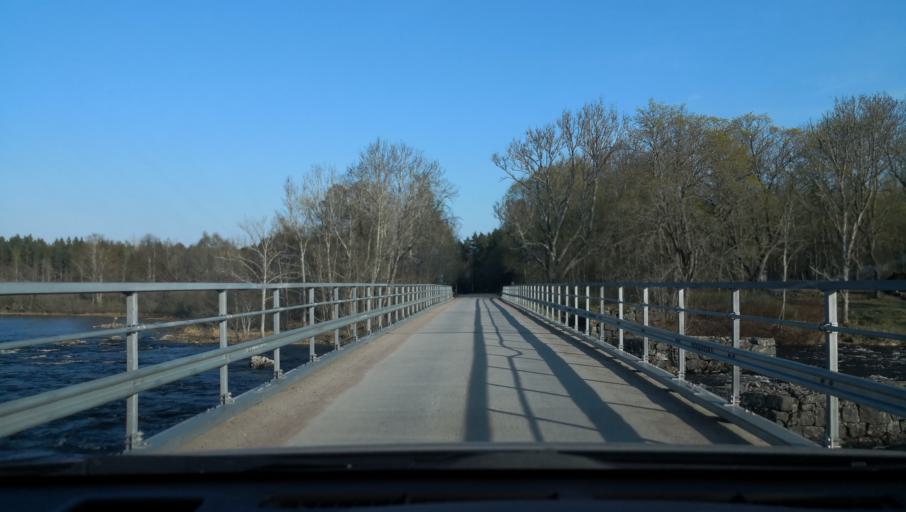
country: SE
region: Uppsala
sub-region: Heby Kommun
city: Tarnsjo
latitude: 60.2676
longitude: 16.9141
